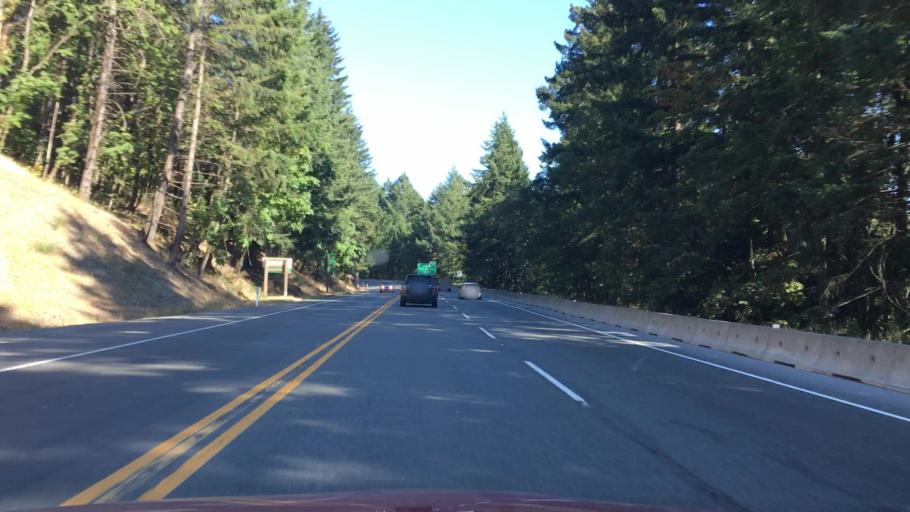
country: CA
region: British Columbia
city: Langford
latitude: 48.4552
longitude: -123.5332
